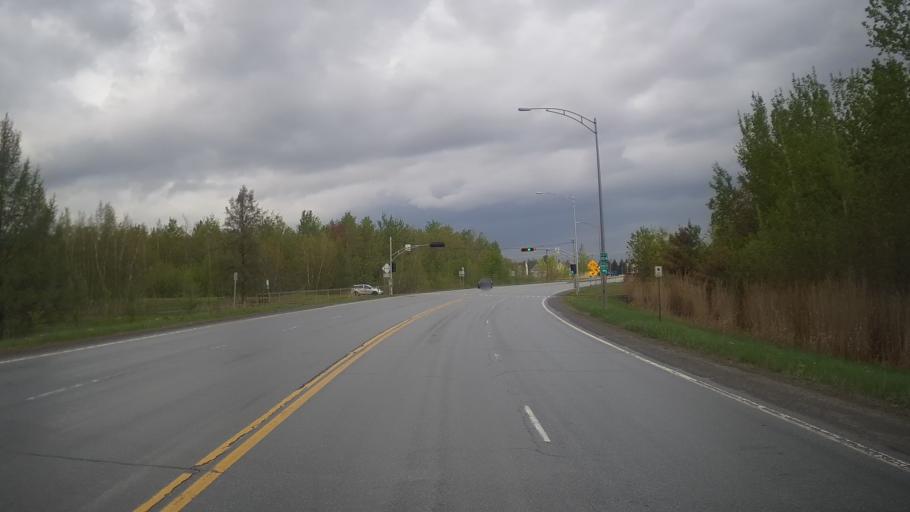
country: CA
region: Quebec
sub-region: Monteregie
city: Farnham
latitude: 45.2839
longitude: -72.9942
